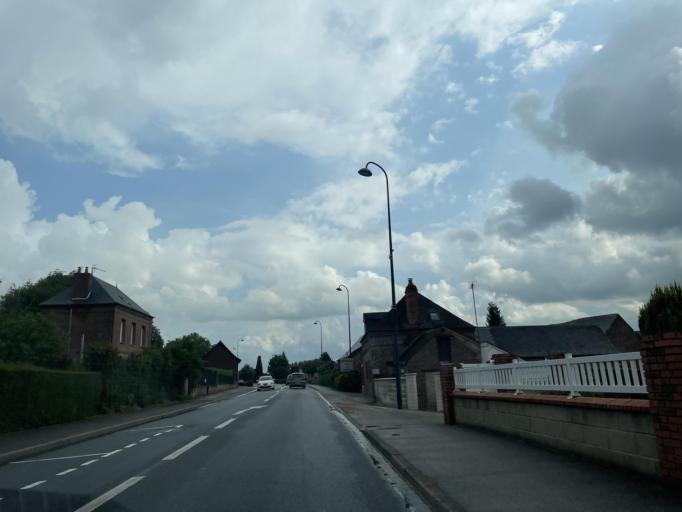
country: FR
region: Haute-Normandie
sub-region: Departement de la Seine-Maritime
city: Envermeu
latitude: 49.8936
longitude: 1.2689
